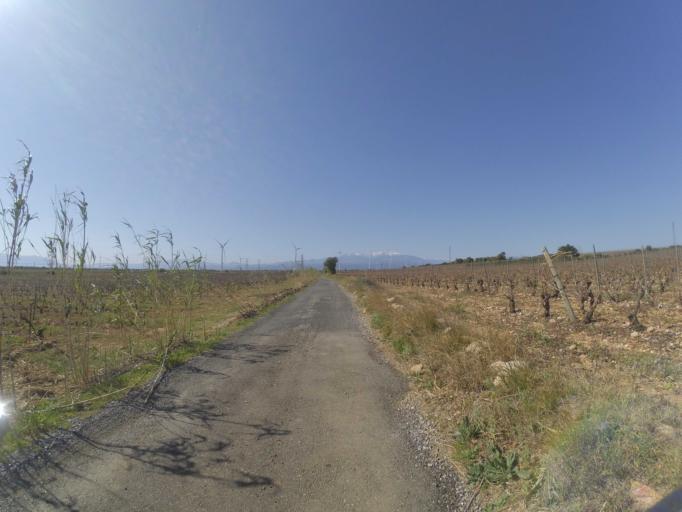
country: FR
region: Languedoc-Roussillon
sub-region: Departement des Pyrenees-Orientales
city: Baixas
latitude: 42.7378
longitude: 2.7924
